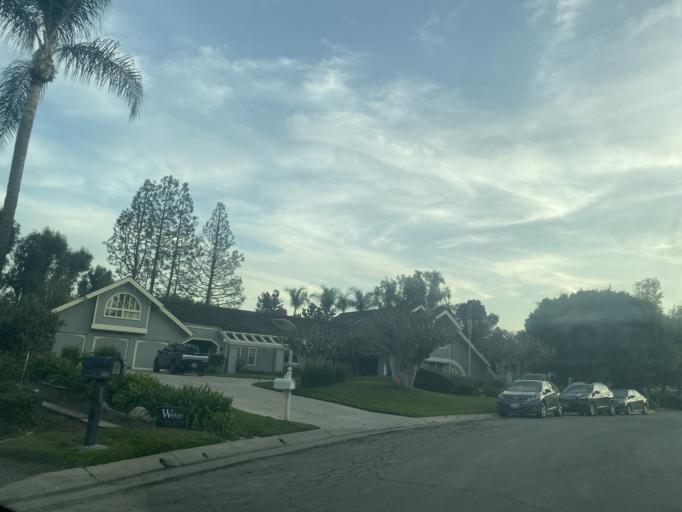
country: US
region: California
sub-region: Orange County
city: Villa Park
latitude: 33.8012
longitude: -117.7810
